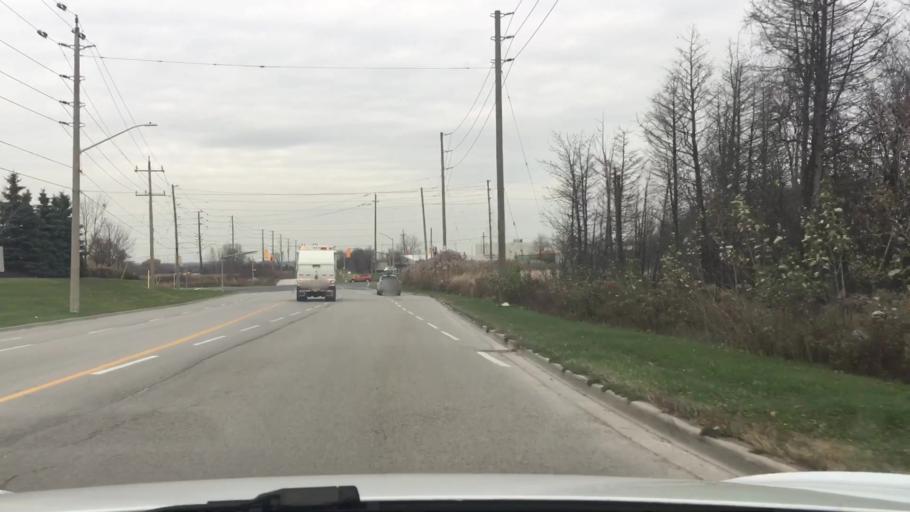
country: CA
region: Ontario
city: Ajax
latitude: 43.8339
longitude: -79.0570
